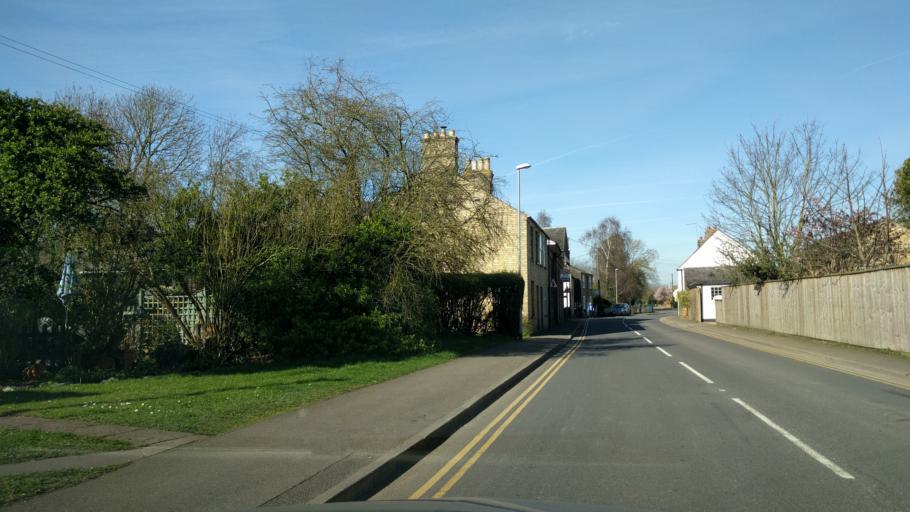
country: GB
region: England
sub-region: Cambridgeshire
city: Earith
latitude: 52.3539
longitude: 0.0312
